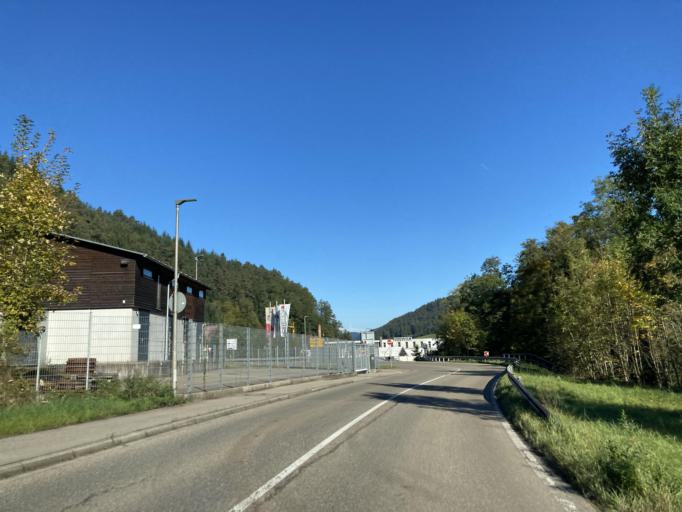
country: DE
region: Baden-Wuerttemberg
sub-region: Freiburg Region
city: Hornberg
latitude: 48.2206
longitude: 8.2236
